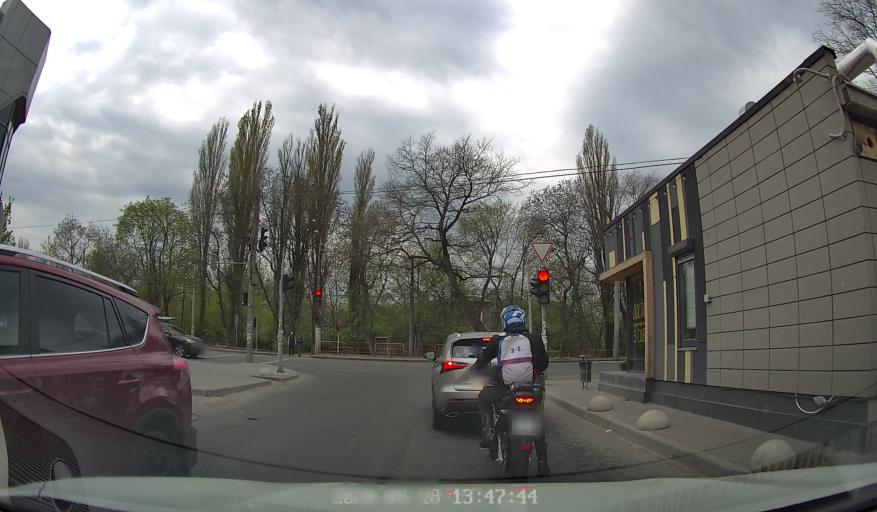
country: NE
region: Zinder
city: Mirriah
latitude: 13.9265
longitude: 9.2177
